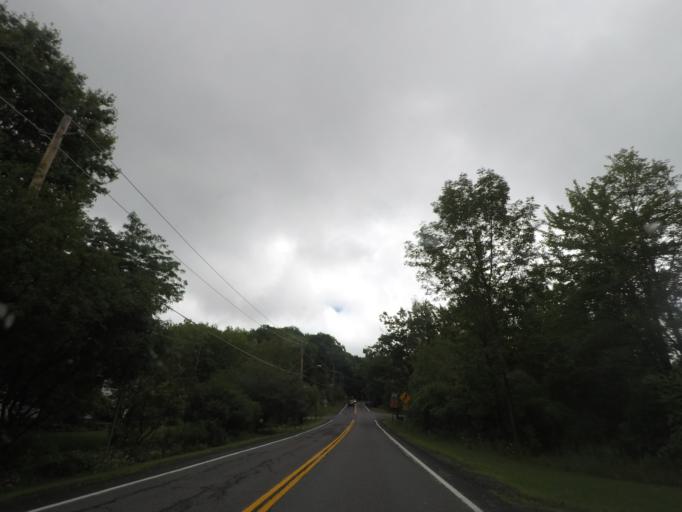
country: US
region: New York
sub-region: Rensselaer County
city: Averill Park
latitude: 42.5799
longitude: -73.4735
